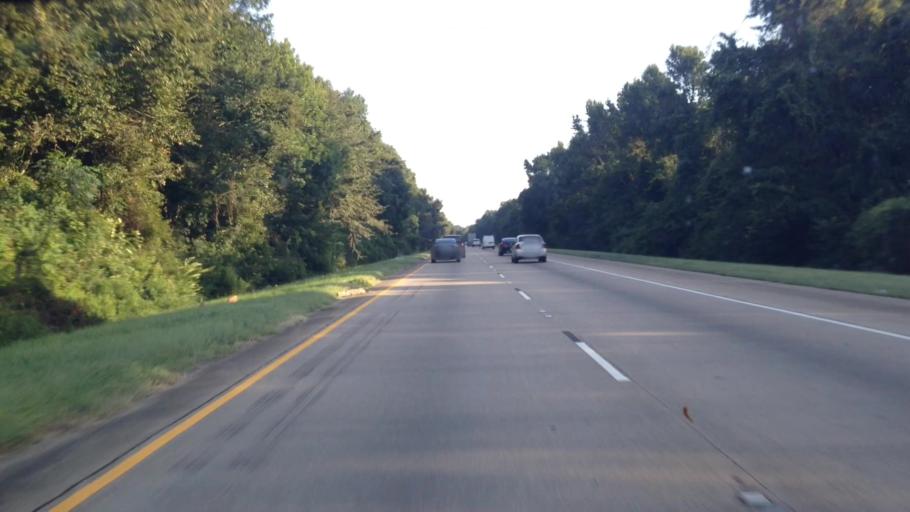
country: US
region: Louisiana
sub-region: Ascension Parish
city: Prairieville
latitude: 30.2955
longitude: -90.9913
